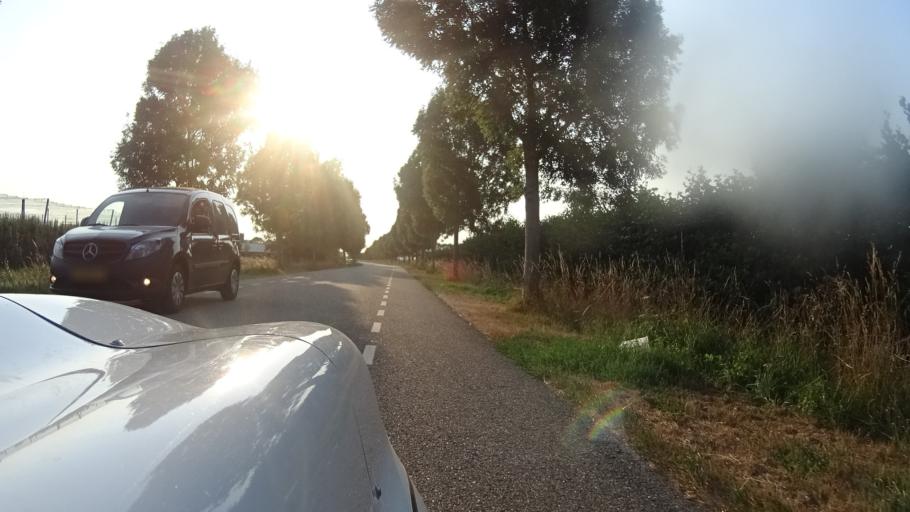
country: NL
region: Gelderland
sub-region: Gemeente Druten
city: Druten
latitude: 51.8440
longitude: 5.5525
